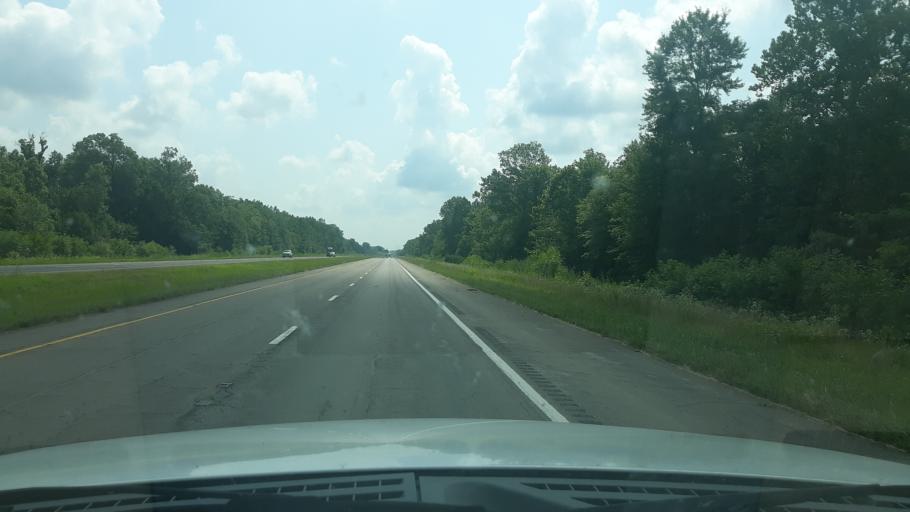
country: US
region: Illinois
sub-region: Saline County
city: Carrier Mills
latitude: 37.7343
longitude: -88.6960
